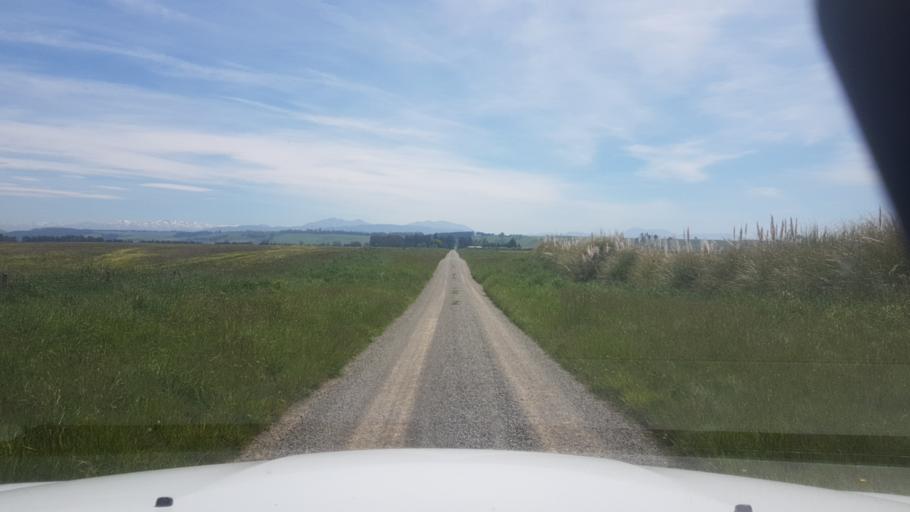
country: NZ
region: Canterbury
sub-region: Timaru District
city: Pleasant Point
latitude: -44.2326
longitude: 171.1672
